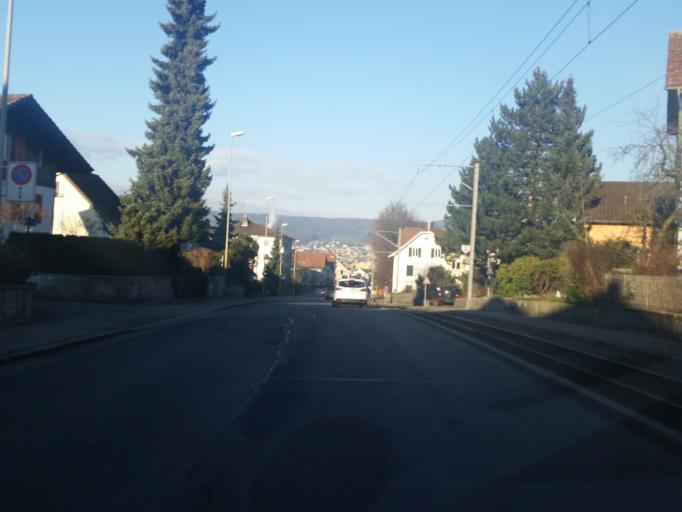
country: CH
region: Zurich
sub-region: Bezirk Dietikon
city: Dietikon / Kreuzacker
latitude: 47.3985
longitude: 8.3994
